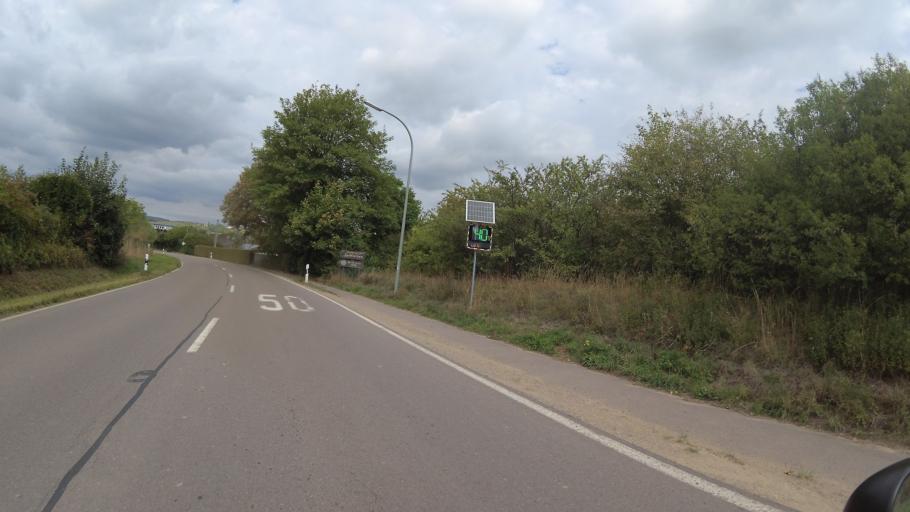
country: FR
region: Lorraine
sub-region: Departement de la Moselle
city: Bliesbruck
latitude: 49.1327
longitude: 7.1390
